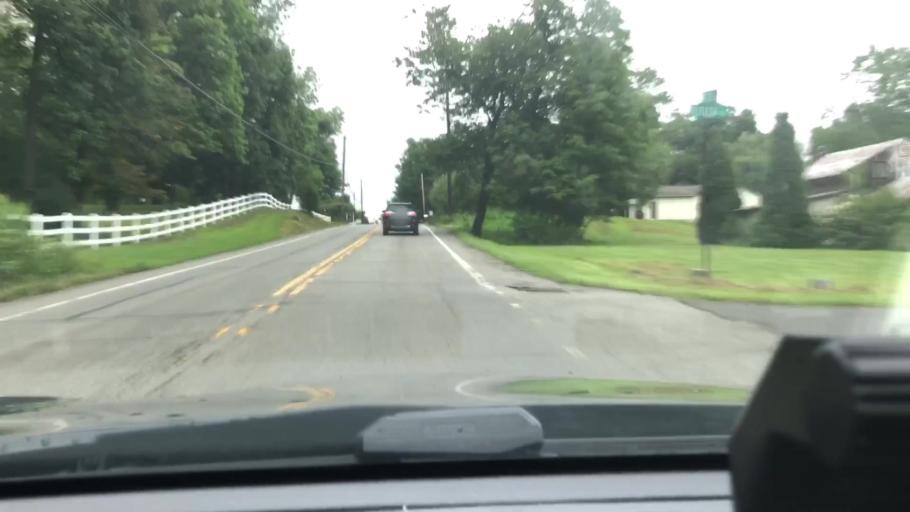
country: US
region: Pennsylvania
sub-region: Montgomery County
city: Gilbertsville
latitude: 40.3318
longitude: -75.5538
